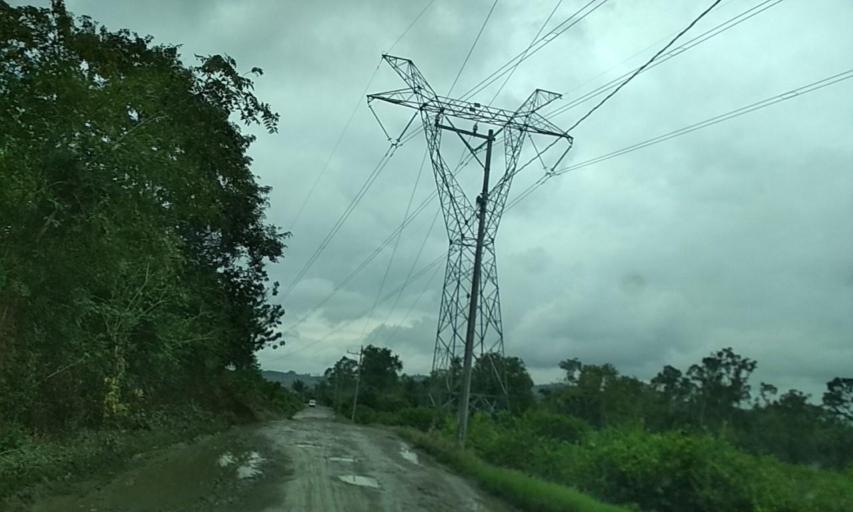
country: MX
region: Puebla
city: Espinal
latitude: 20.3132
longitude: -97.4153
